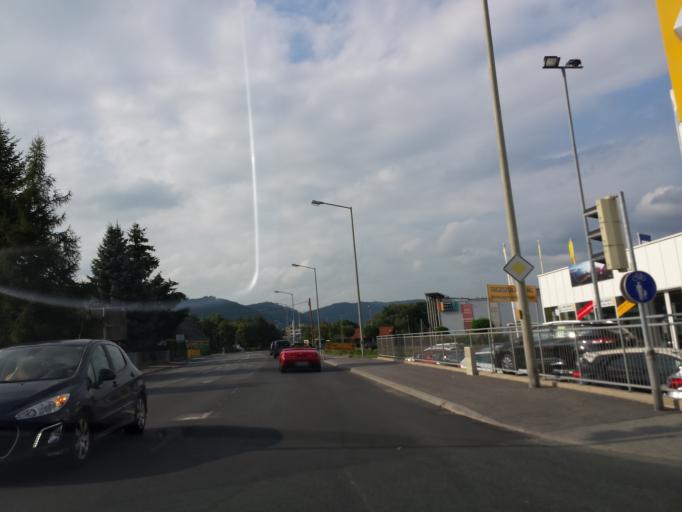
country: AT
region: Styria
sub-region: Graz Stadt
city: Wetzelsdorf
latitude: 47.0307
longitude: 15.4008
